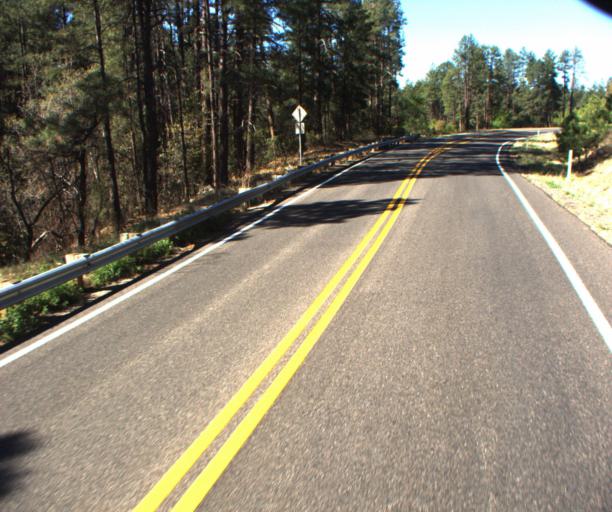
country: US
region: Arizona
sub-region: Yavapai County
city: Prescott
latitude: 34.4972
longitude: -112.4843
